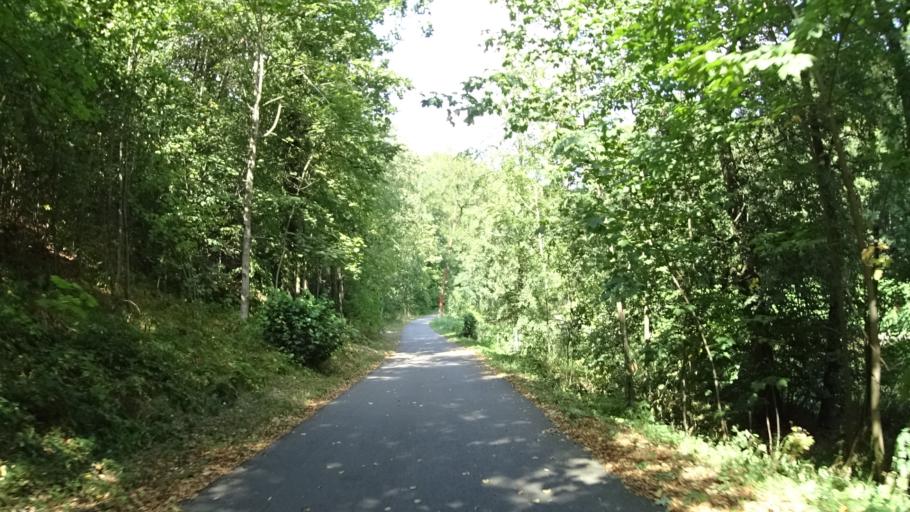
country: DE
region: Saxony
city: Hirschfelde
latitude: 50.9587
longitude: 14.8968
